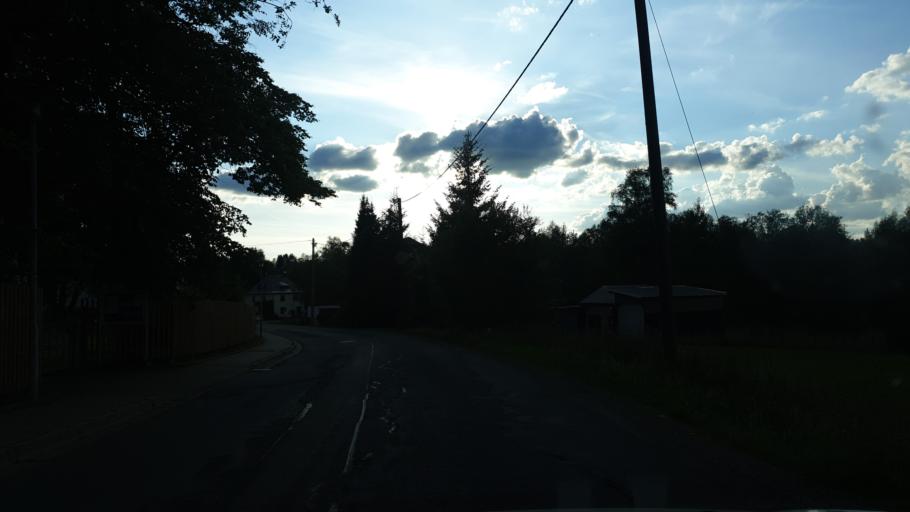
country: DE
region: Saxony
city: Hammerbrucke
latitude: 50.4354
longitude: 12.4165
